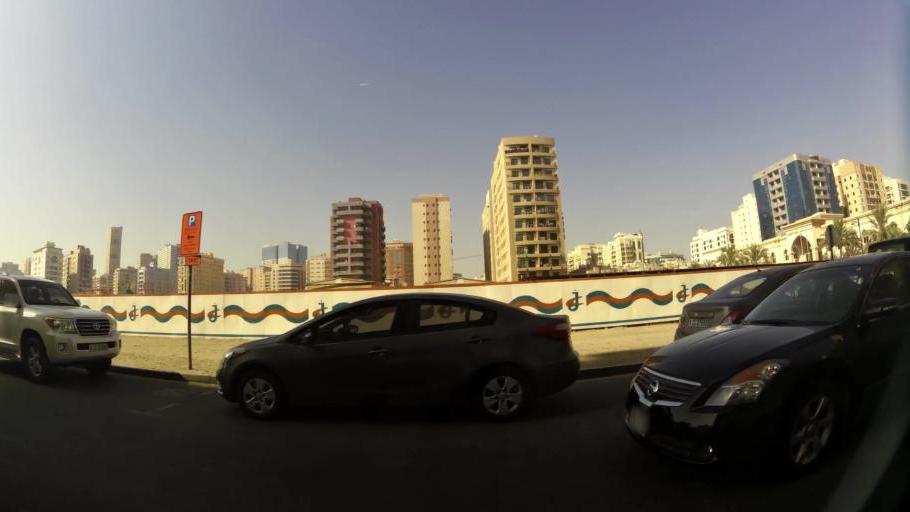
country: AE
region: Ash Shariqah
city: Sharjah
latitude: 25.2910
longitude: 55.3777
